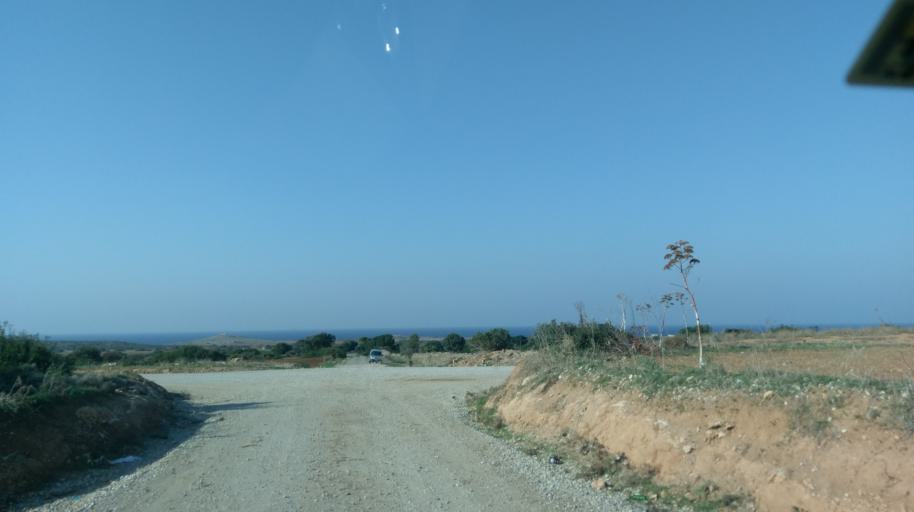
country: CY
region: Ammochostos
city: Leonarisso
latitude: 35.5456
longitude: 34.1857
